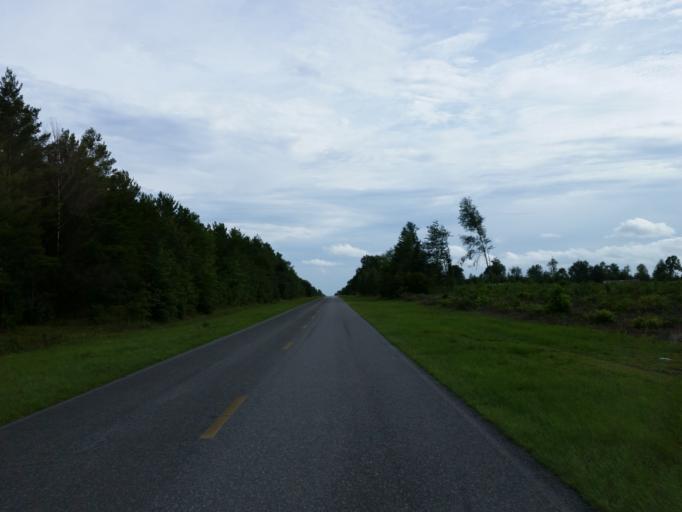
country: US
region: Florida
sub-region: Hamilton County
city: Jasper
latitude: 30.4614
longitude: -83.1508
